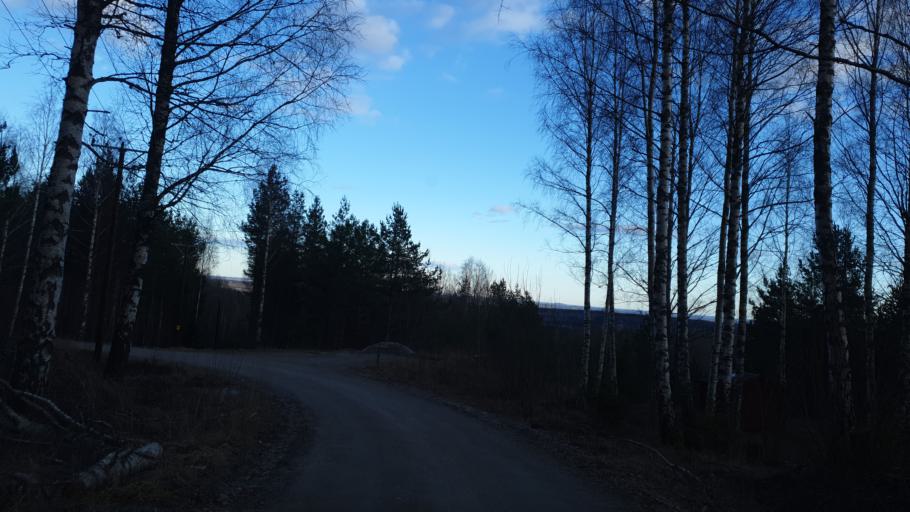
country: SE
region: OErebro
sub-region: Orebro Kommun
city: Garphyttan
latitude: 59.3623
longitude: 14.9726
